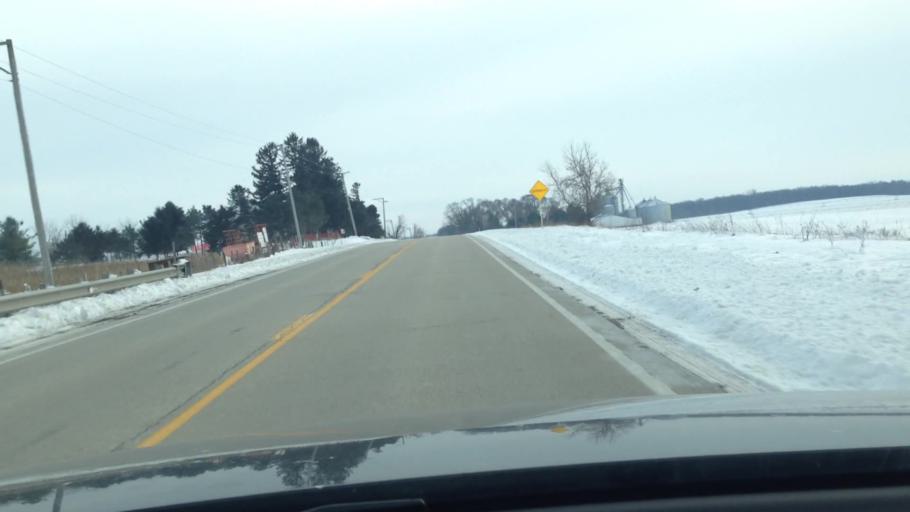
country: US
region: Illinois
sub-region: McHenry County
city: Hebron
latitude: 42.4055
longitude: -88.4383
